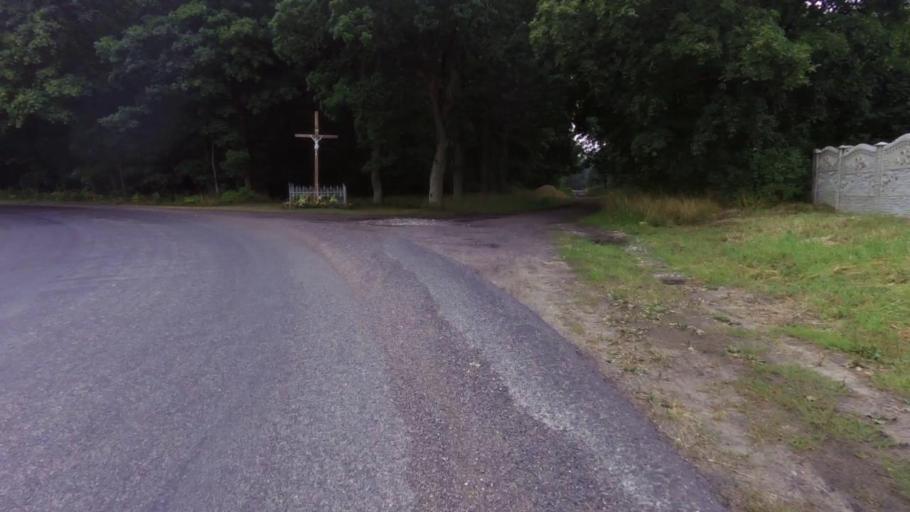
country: PL
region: West Pomeranian Voivodeship
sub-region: Powiat choszczenski
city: Choszczno
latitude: 53.2229
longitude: 15.3794
